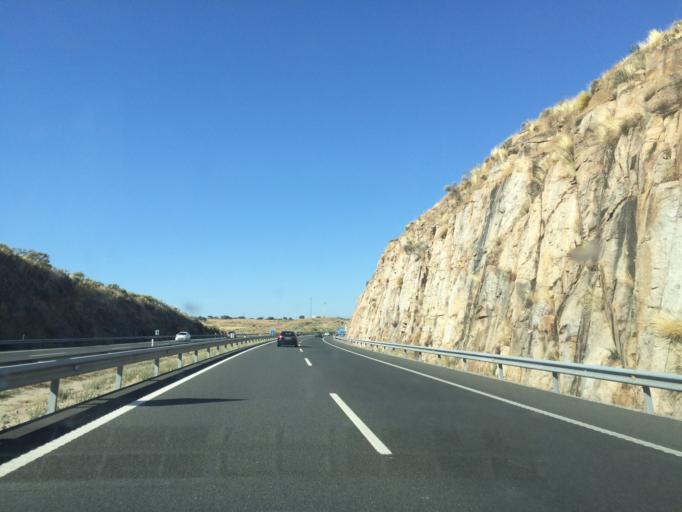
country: ES
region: Extremadura
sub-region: Provincia de Caceres
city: Navalmoral de la Mata
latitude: 39.8791
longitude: -5.5400
